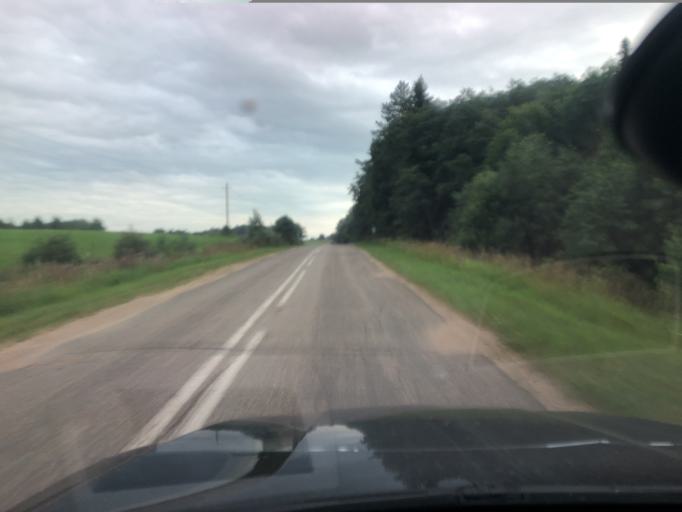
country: RU
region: Jaroslavl
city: Pereslavl'-Zalesskiy
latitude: 57.0191
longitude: 38.9517
